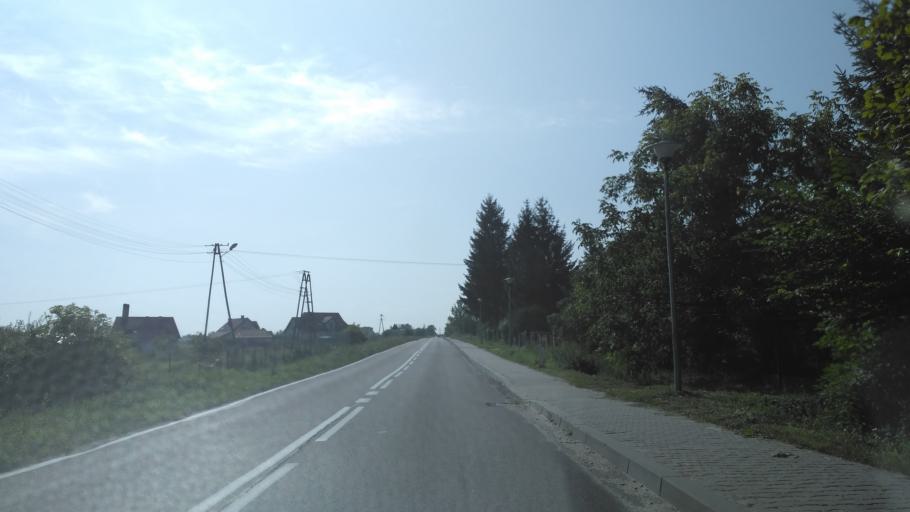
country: PL
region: Lublin Voivodeship
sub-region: Powiat leczynski
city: Cycow
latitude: 51.1896
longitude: 23.1633
